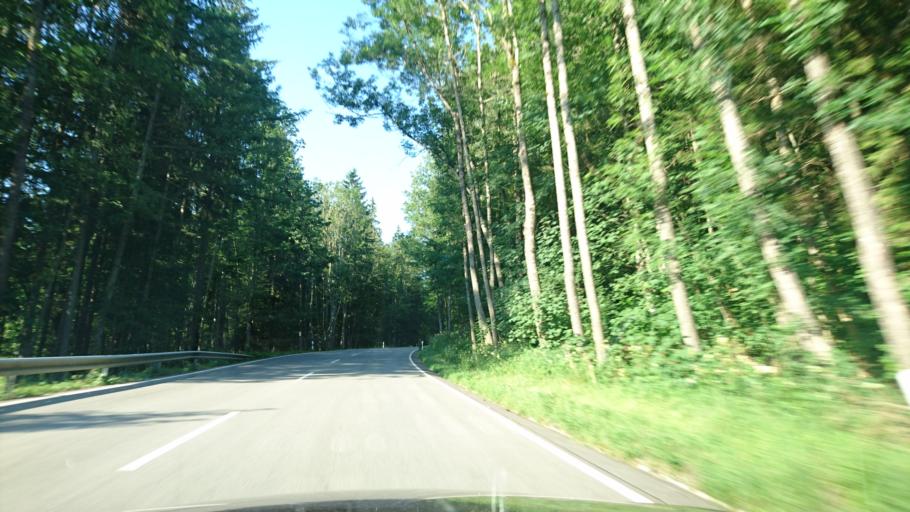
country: DE
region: Bavaria
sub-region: Upper Bavaria
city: Ruhpolding
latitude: 47.7459
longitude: 12.6715
